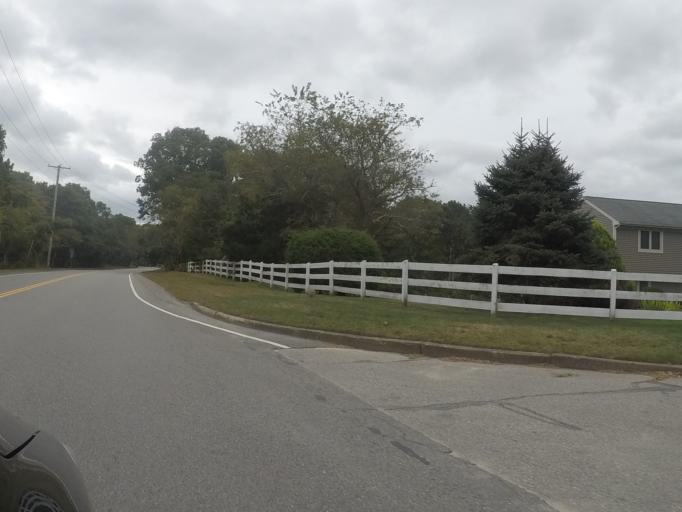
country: US
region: Massachusetts
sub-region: Bristol County
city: Smith Mills
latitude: 41.5884
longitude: -71.0009
